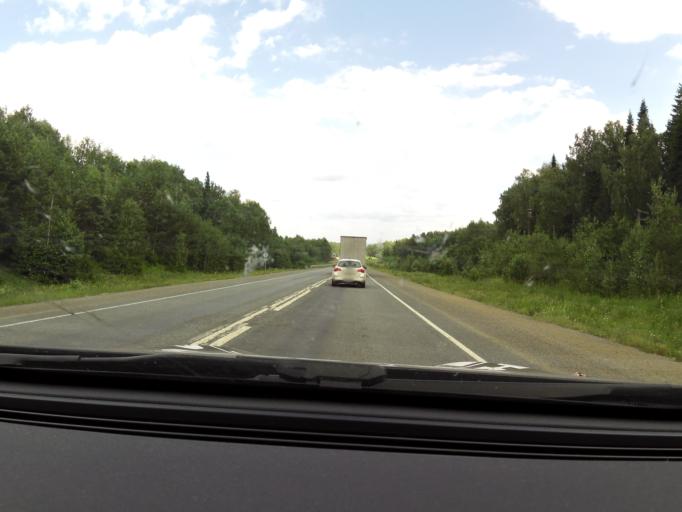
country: RU
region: Sverdlovsk
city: Bisert'
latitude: 56.8277
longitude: 59.0054
